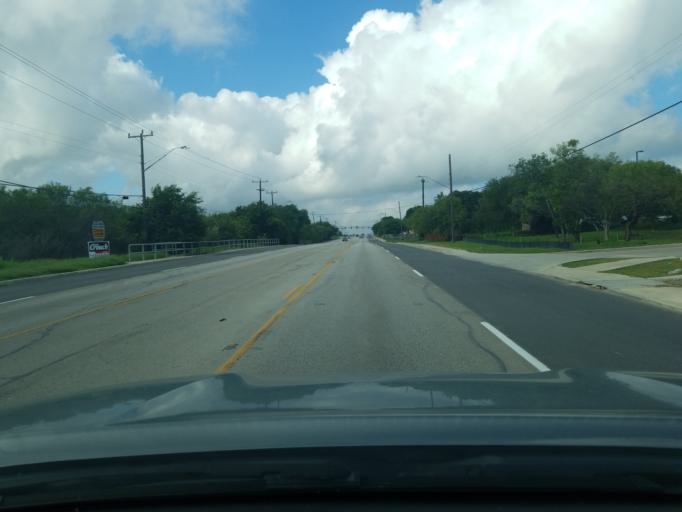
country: US
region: Texas
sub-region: Bexar County
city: Live Oak
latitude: 29.5853
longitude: -98.3626
